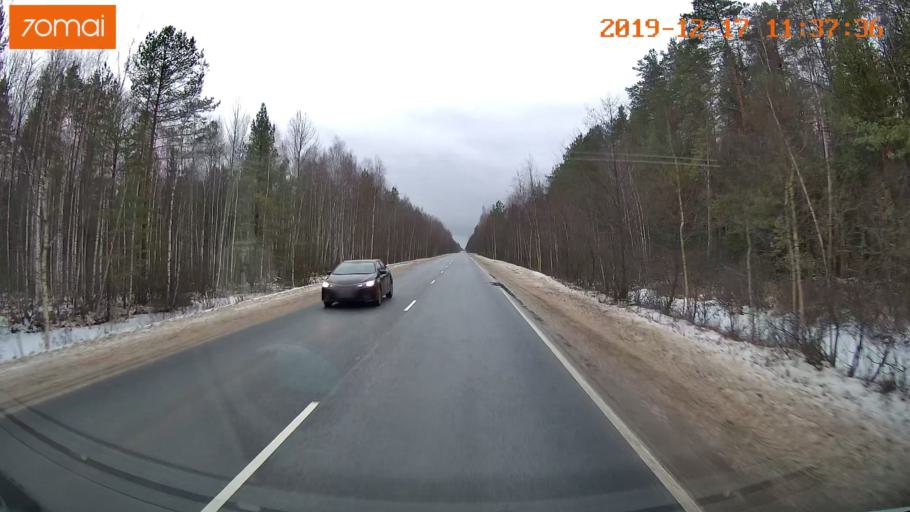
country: RU
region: Vladimir
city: Velikodvorskiy
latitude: 55.3577
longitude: 40.6791
